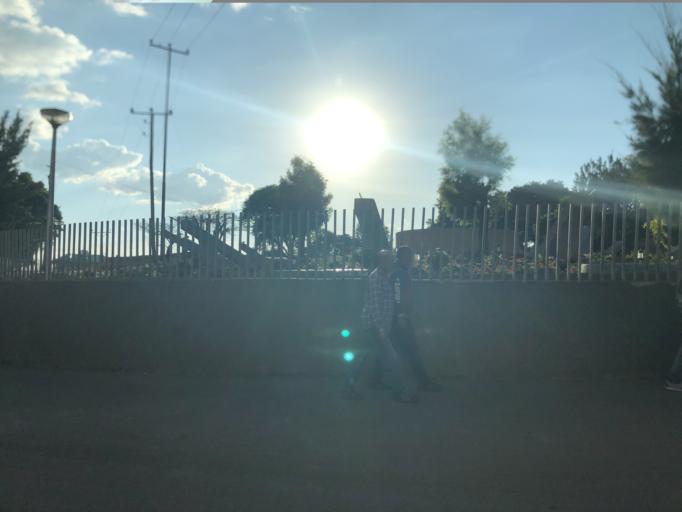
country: ET
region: Amhara
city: Gondar
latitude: 12.6180
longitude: 37.4708
